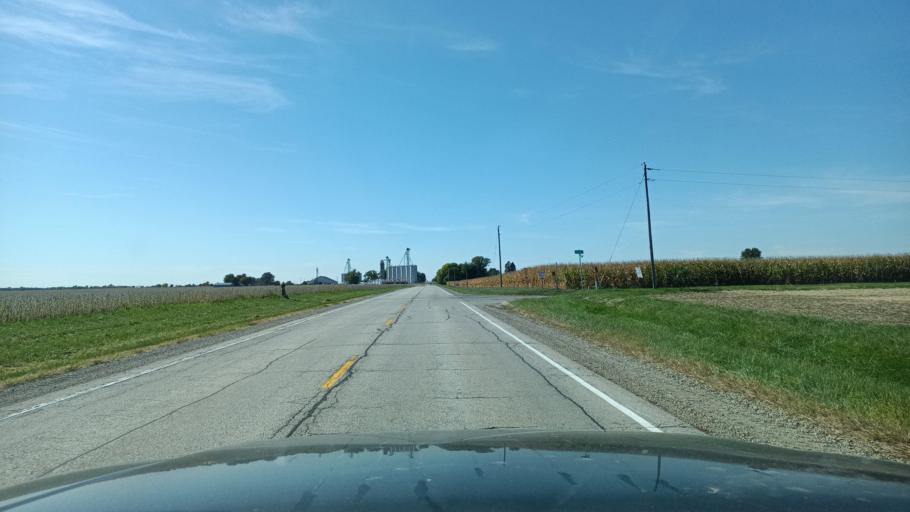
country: US
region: Illinois
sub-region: De Witt County
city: Farmer City
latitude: 40.2238
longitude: -88.7075
